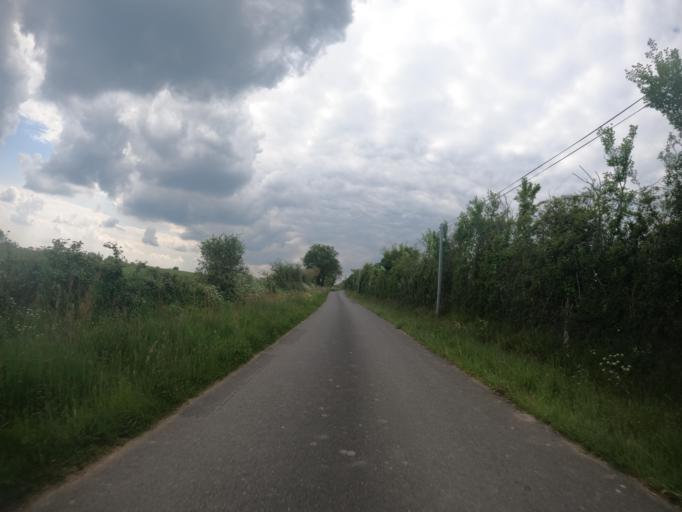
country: FR
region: Poitou-Charentes
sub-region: Departement des Deux-Sevres
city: Saint-Varent
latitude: 46.8669
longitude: -0.3086
